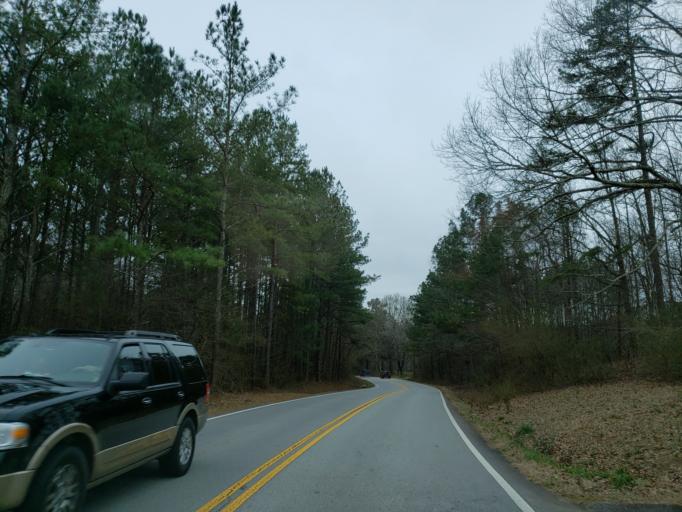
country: US
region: Georgia
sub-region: Paulding County
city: Hiram
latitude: 33.9169
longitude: -84.7235
